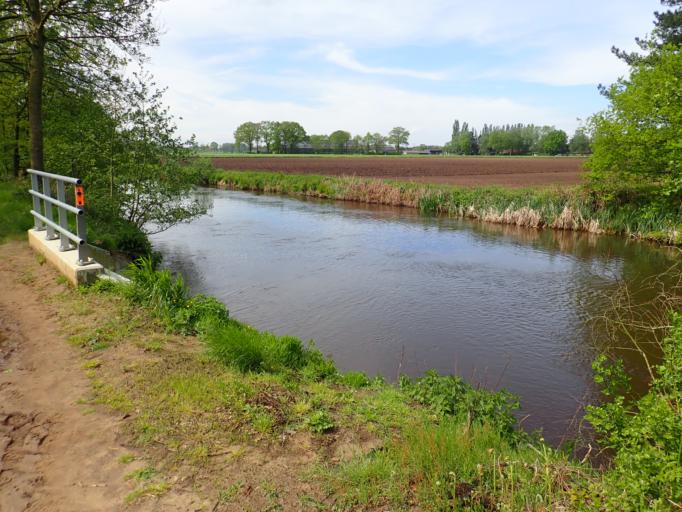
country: BE
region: Flanders
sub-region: Provincie Antwerpen
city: Lille
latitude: 51.2126
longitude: 4.8378
